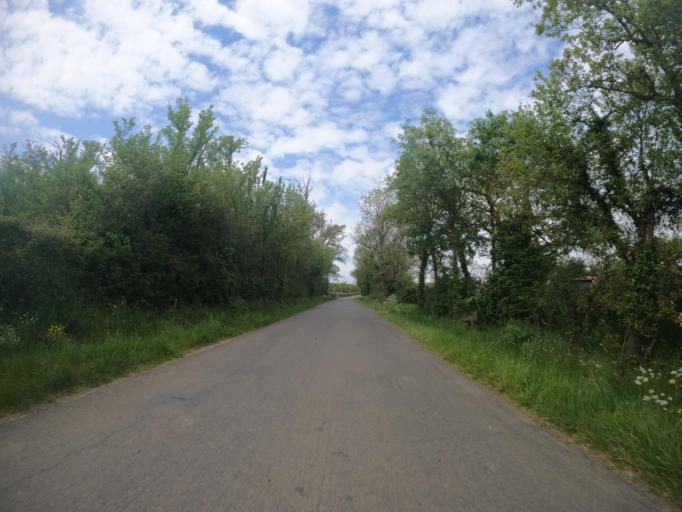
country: FR
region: Poitou-Charentes
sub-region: Departement des Deux-Sevres
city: Saint-Varent
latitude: 46.8807
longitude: -0.2947
